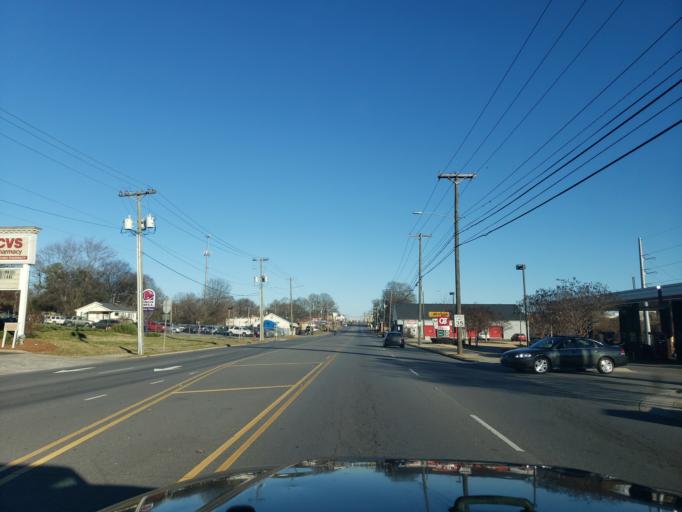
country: US
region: North Carolina
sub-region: Gaston County
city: Gastonia
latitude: 35.2598
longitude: -81.2152
